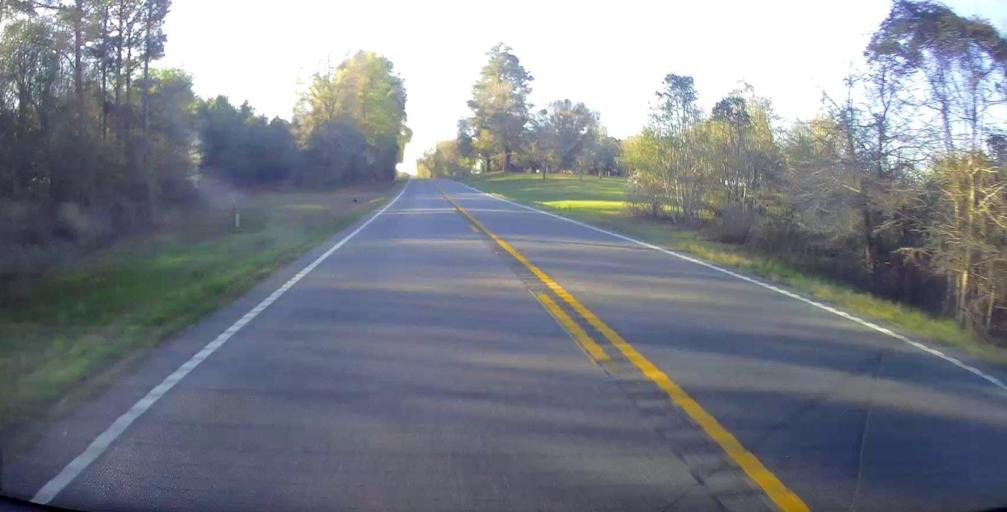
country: US
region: Georgia
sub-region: Pulaski County
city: Hawkinsville
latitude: 32.2385
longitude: -83.4019
